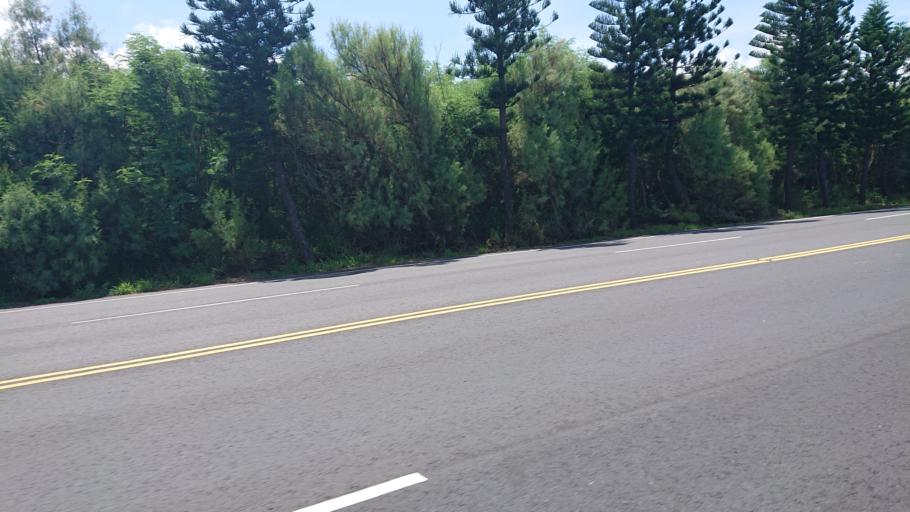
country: TW
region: Taiwan
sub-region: Penghu
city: Ma-kung
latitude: 23.6372
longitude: 119.5972
